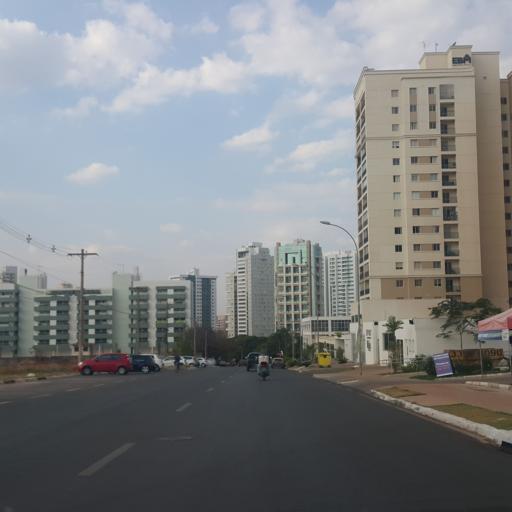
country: BR
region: Federal District
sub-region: Brasilia
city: Brasilia
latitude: -15.8471
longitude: -48.0327
